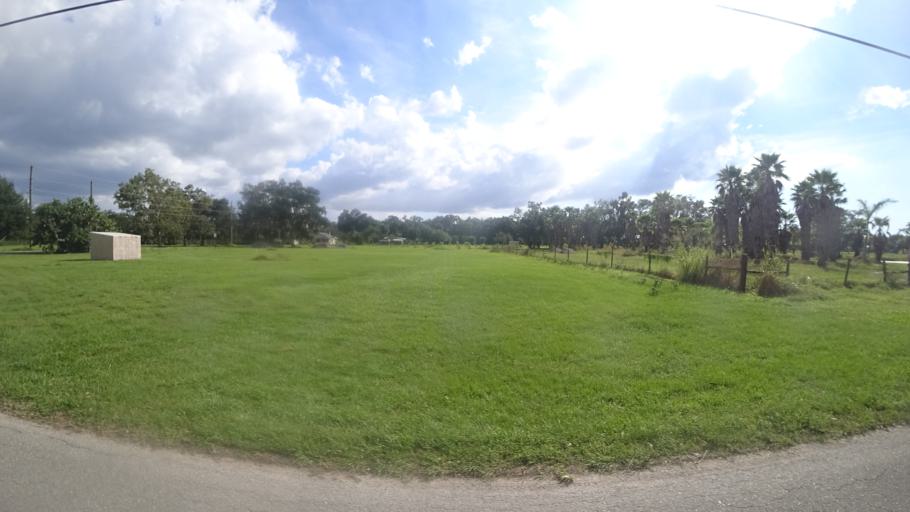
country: US
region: Florida
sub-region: Manatee County
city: Memphis
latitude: 27.5795
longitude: -82.5813
